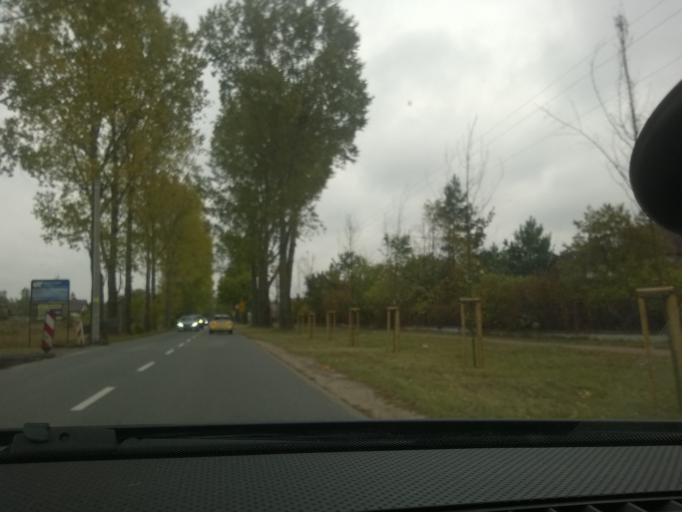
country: PL
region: Masovian Voivodeship
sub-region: Powiat pruszkowski
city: Nadarzyn
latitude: 52.1076
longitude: 20.8015
